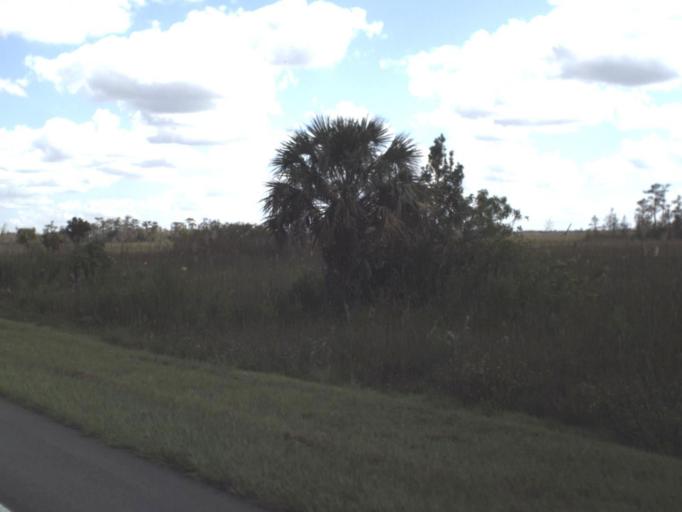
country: US
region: Florida
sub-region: Collier County
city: Marco
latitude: 25.8757
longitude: -81.2188
